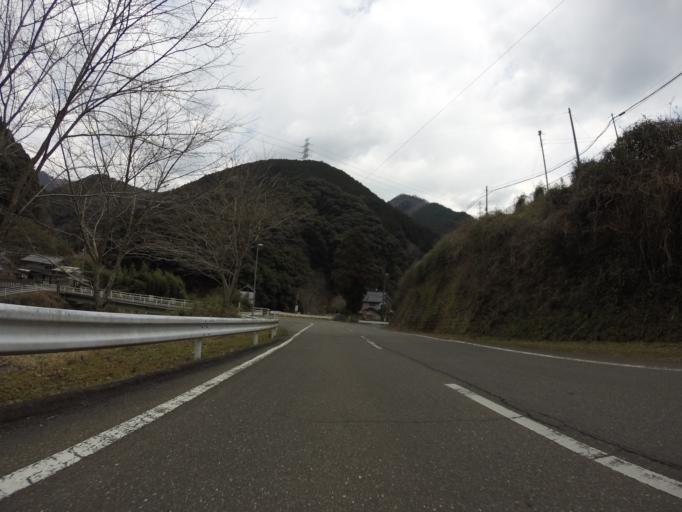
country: JP
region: Shizuoka
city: Shizuoka-shi
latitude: 35.0658
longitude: 138.3306
